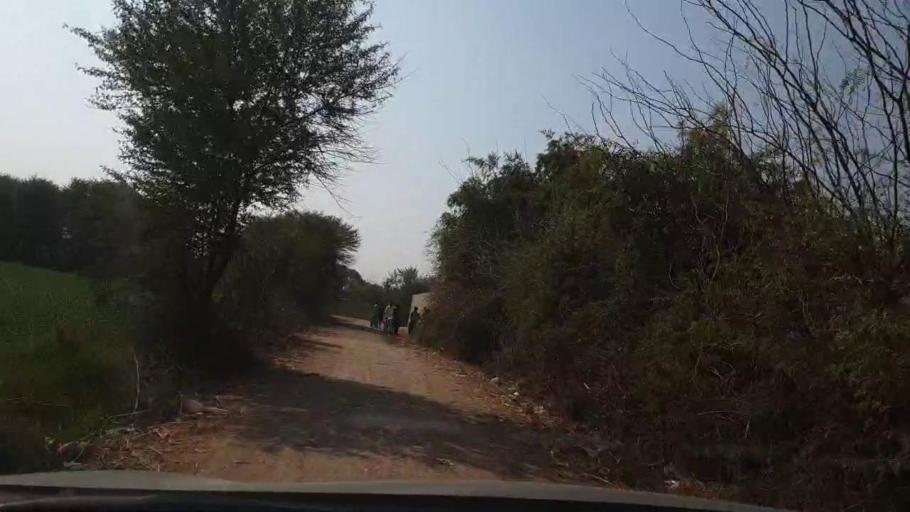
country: PK
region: Sindh
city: Tando Allahyar
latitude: 25.5336
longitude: 68.7685
